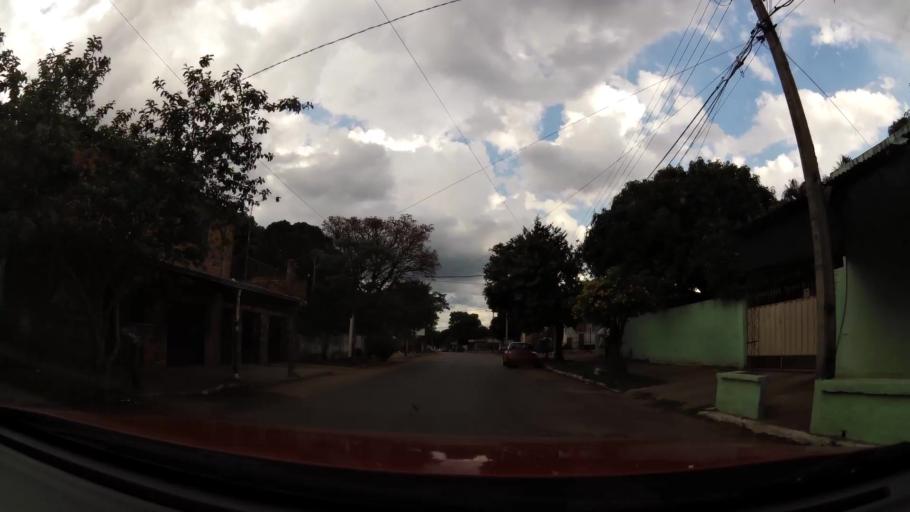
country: PY
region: Central
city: Fernando de la Mora
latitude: -25.3376
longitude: -57.5531
